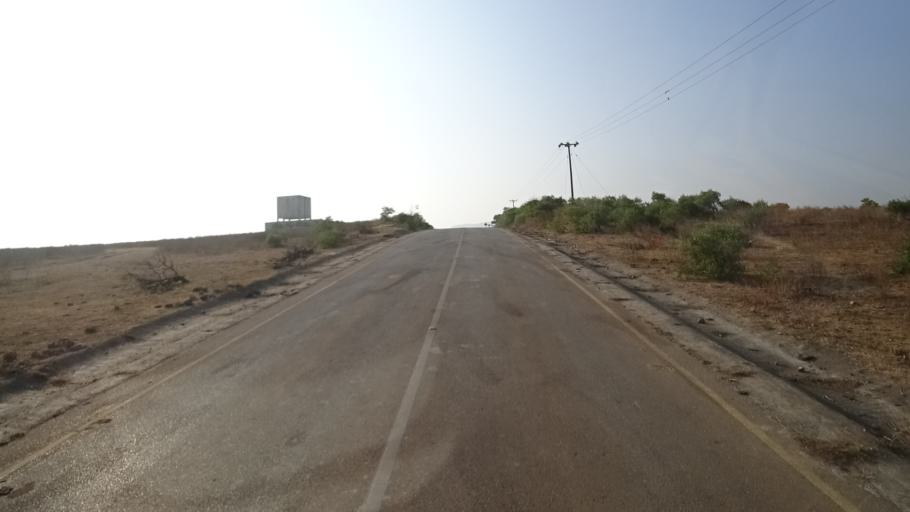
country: YE
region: Al Mahrah
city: Hawf
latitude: 16.7459
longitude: 53.3472
